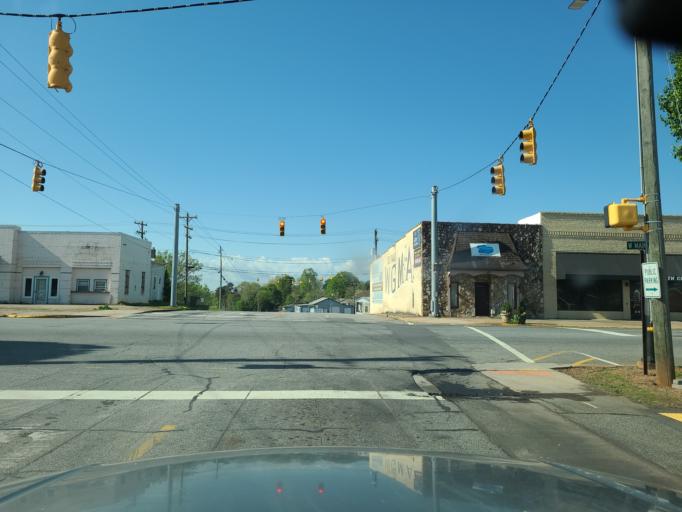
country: US
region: North Carolina
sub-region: Rutherford County
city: Spindale
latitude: 35.3583
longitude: -81.9327
